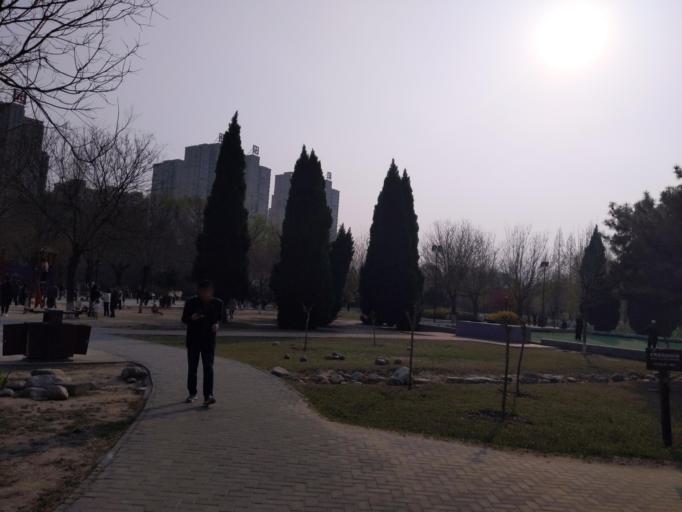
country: CN
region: Henan Sheng
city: Puyang
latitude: 35.7513
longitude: 115.0266
